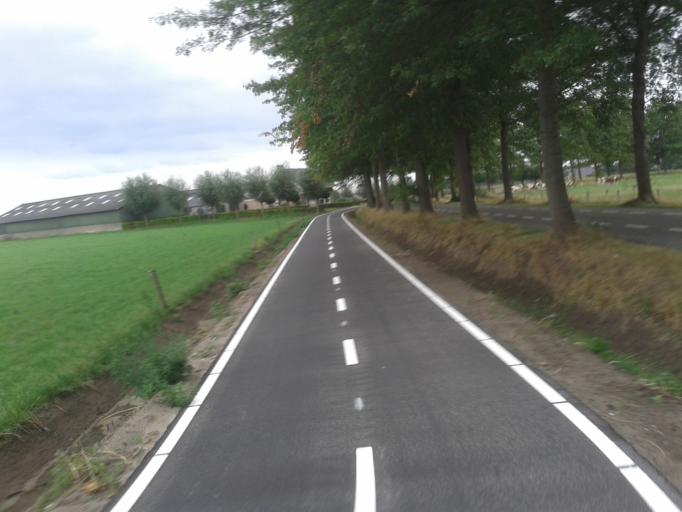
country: NL
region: North Brabant
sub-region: Gemeente Oisterwijk
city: Oisterwijk
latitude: 51.5159
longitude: 5.1953
